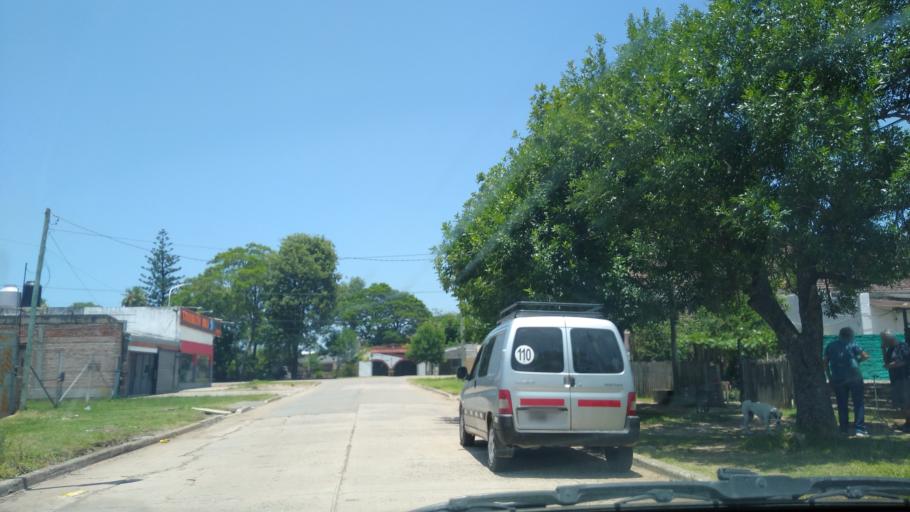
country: AR
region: Chaco
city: Barranqueras
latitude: -27.4905
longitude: -58.9411
